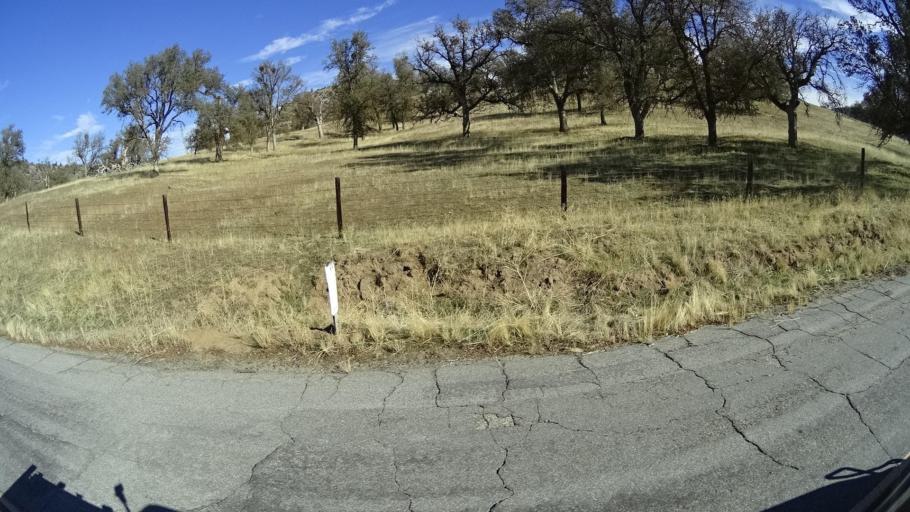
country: US
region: California
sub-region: Kern County
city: Alta Sierra
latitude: 35.6231
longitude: -118.7457
